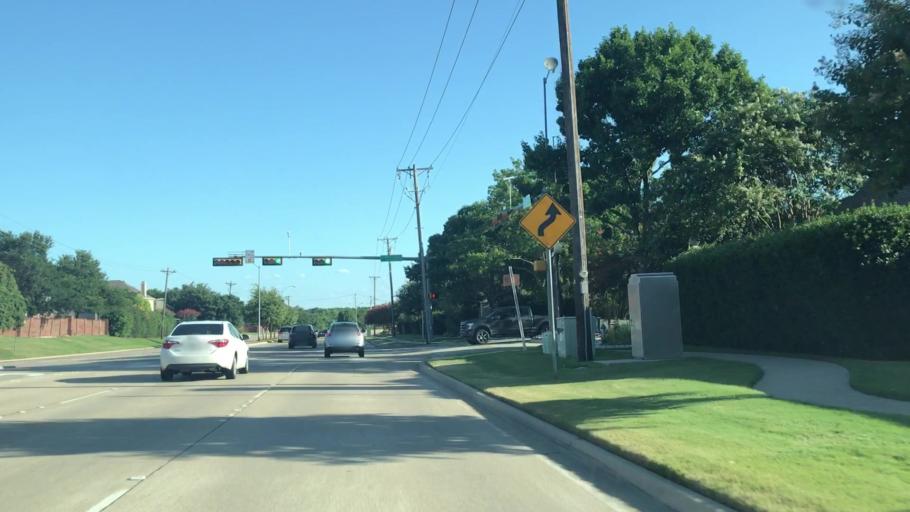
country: US
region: Texas
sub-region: Collin County
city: Allen
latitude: 33.0936
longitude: -96.7336
